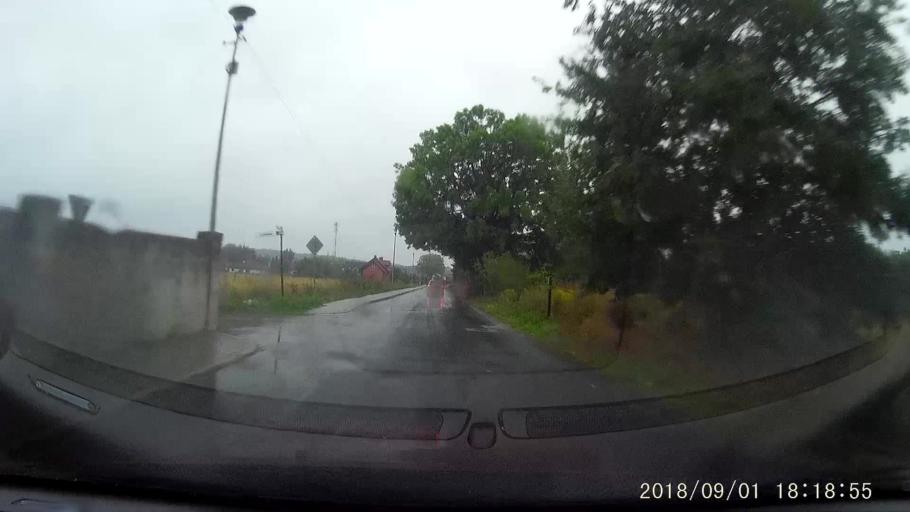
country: PL
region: Lower Silesian Voivodeship
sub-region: Powiat zgorzelecki
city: Piensk
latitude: 51.2574
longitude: 15.0458
